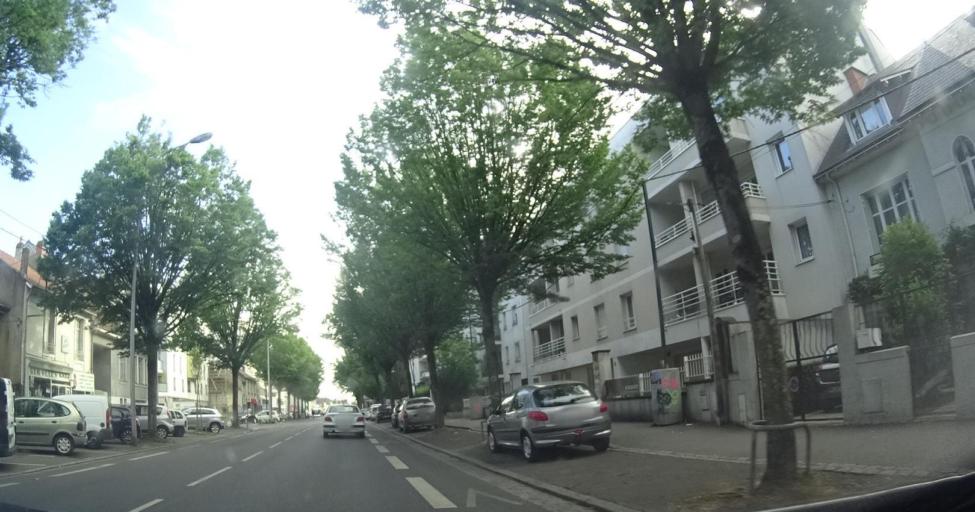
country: FR
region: Pays de la Loire
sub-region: Departement de la Loire-Atlantique
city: Nantes
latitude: 47.2358
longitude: -1.5343
